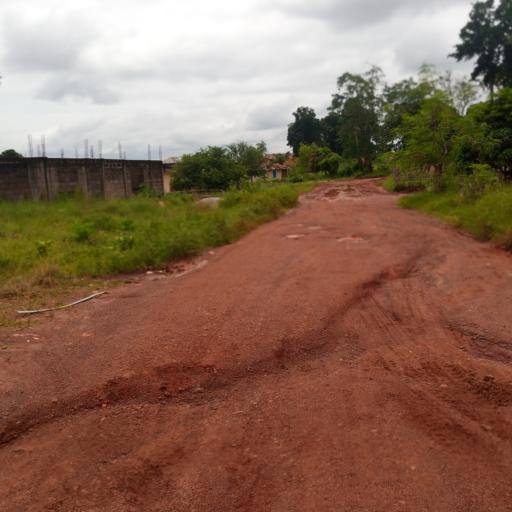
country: SL
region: Eastern Province
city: Kenema
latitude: 7.8862
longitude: -11.1928
